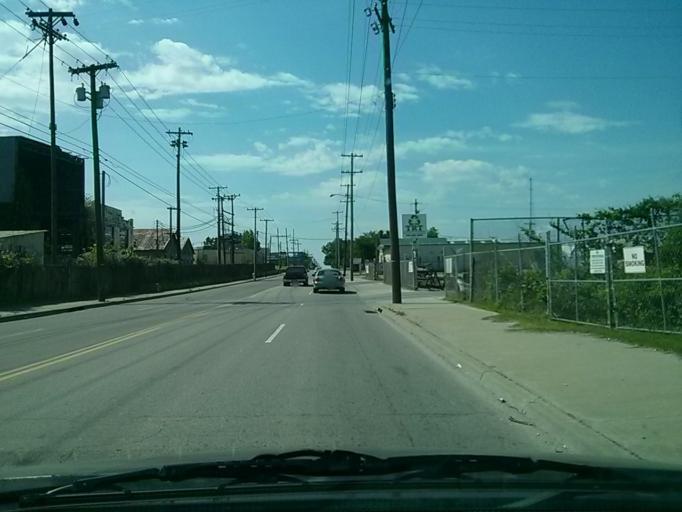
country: US
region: Oklahoma
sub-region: Tulsa County
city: Tulsa
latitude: 36.1716
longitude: -95.9756
